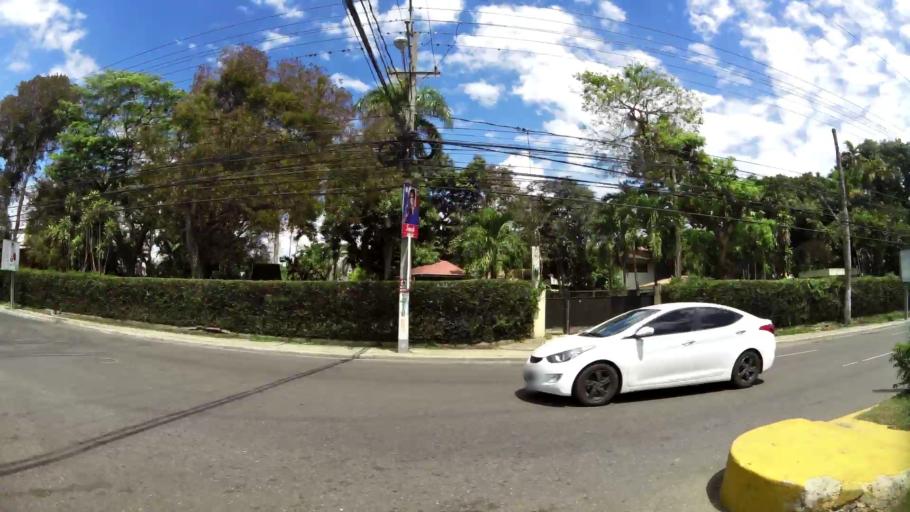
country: DO
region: Santiago
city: Santiago de los Caballeros
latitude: 19.4586
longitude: -70.6724
